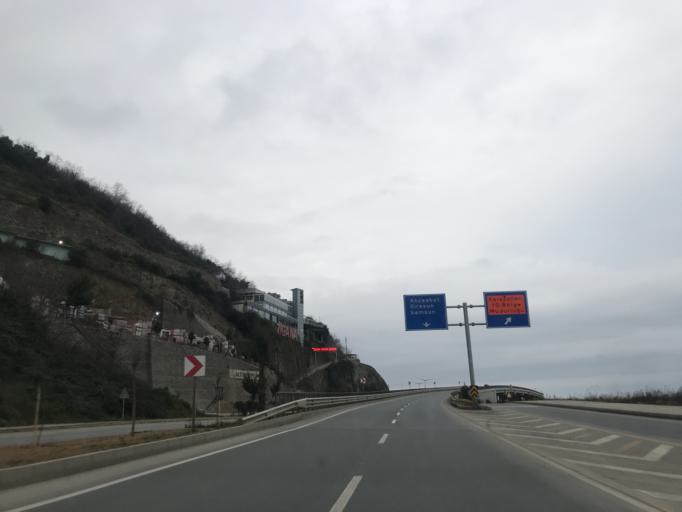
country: TR
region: Trabzon
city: Akcaabat
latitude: 41.0001
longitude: 39.6380
